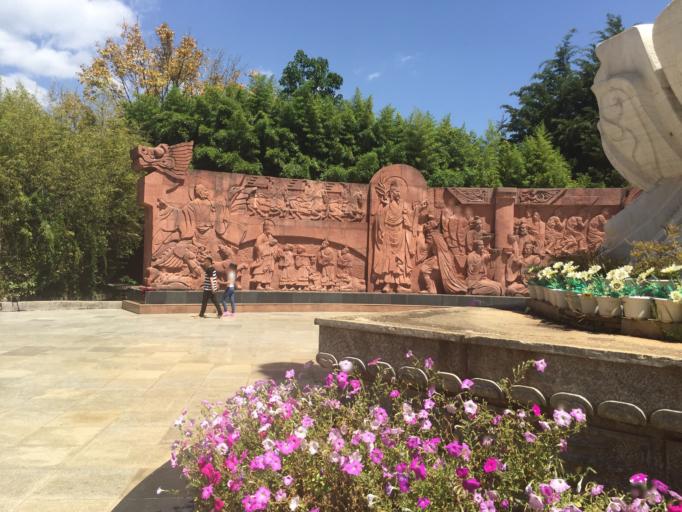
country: CN
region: Yunnan
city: Yuhu
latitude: 25.9051
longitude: 100.1905
